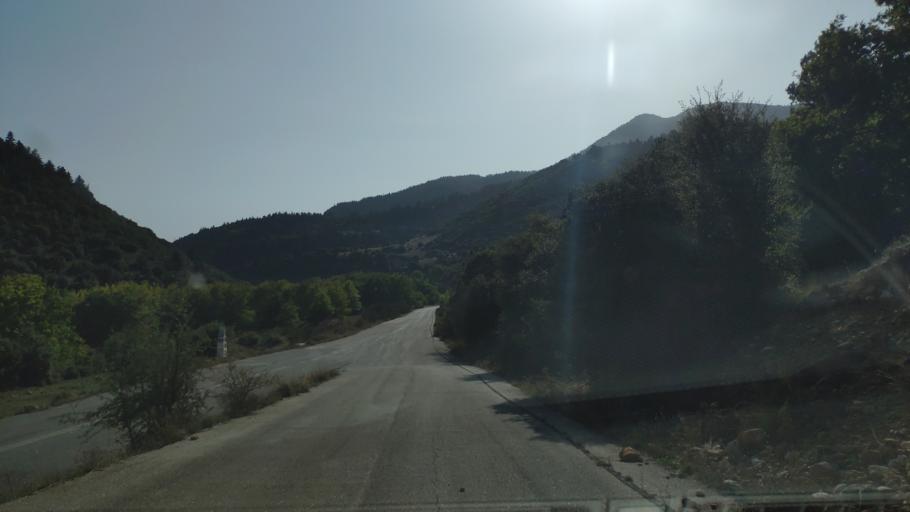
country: GR
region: West Greece
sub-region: Nomos Achaias
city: Aiyira
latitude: 37.9849
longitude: 22.3583
